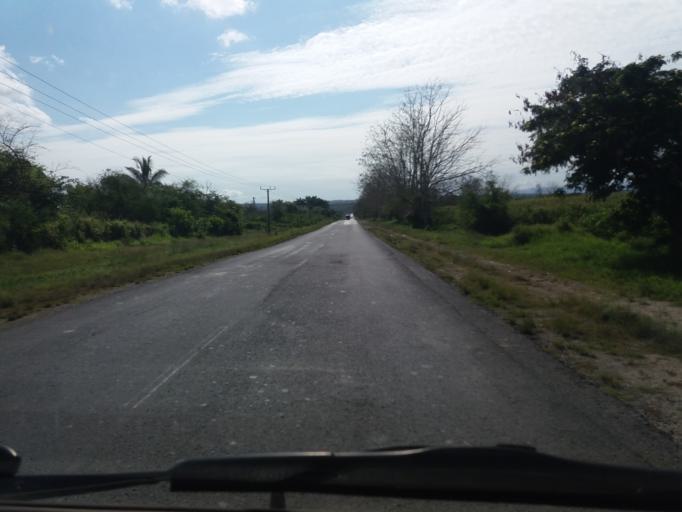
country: CU
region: Cienfuegos
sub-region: Municipio de Cienfuegos
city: Cienfuegos
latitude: 22.1657
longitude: -80.3866
